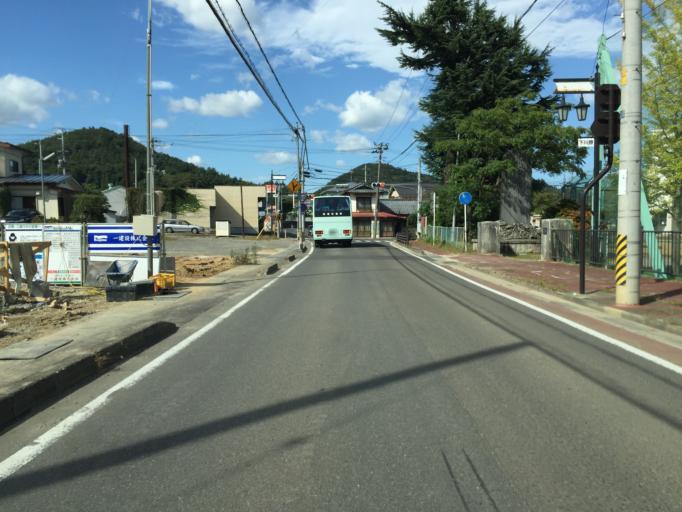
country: JP
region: Fukushima
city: Hobaramachi
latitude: 37.7879
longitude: 140.5942
